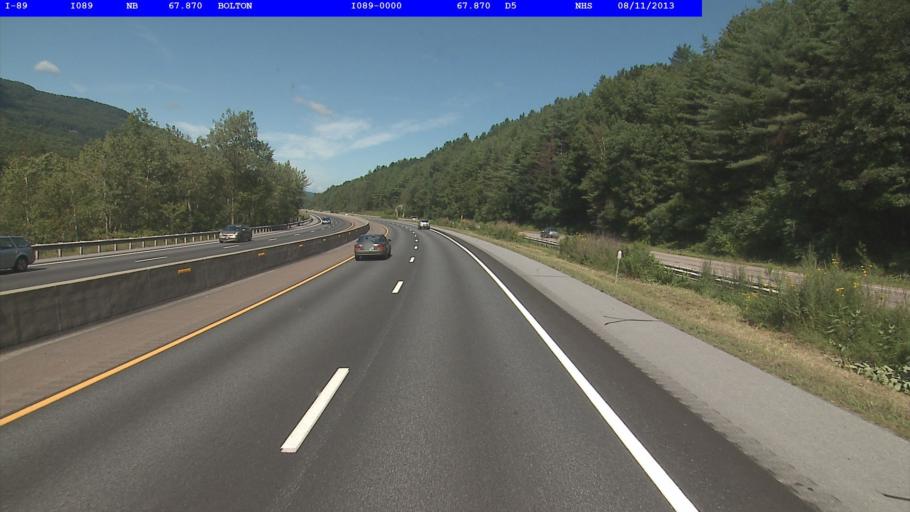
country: US
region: Vermont
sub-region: Washington County
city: Waterbury
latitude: 44.3608
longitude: -72.8273
